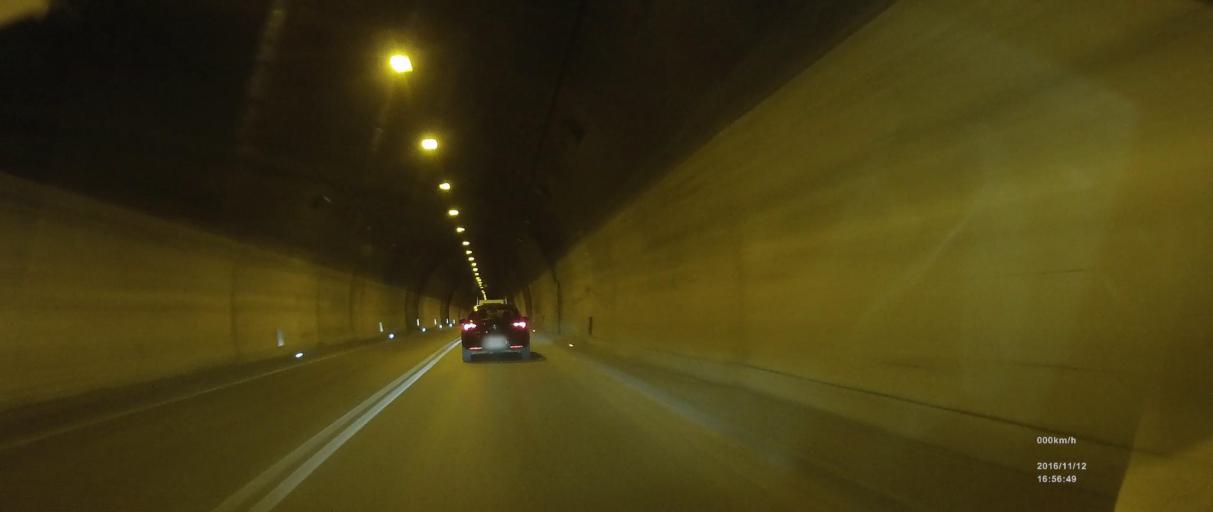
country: HR
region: Splitsko-Dalmatinska
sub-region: Grad Split
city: Split
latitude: 43.5069
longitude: 16.4245
